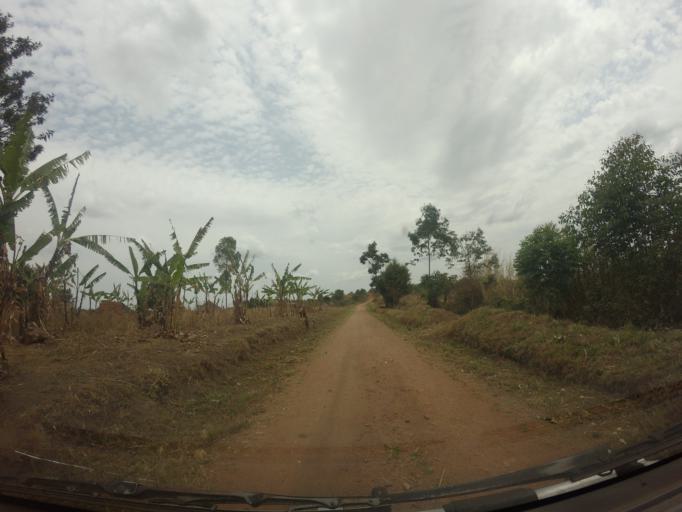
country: UG
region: Northern Region
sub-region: Arua District
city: Arua
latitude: 2.8219
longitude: 30.9025
